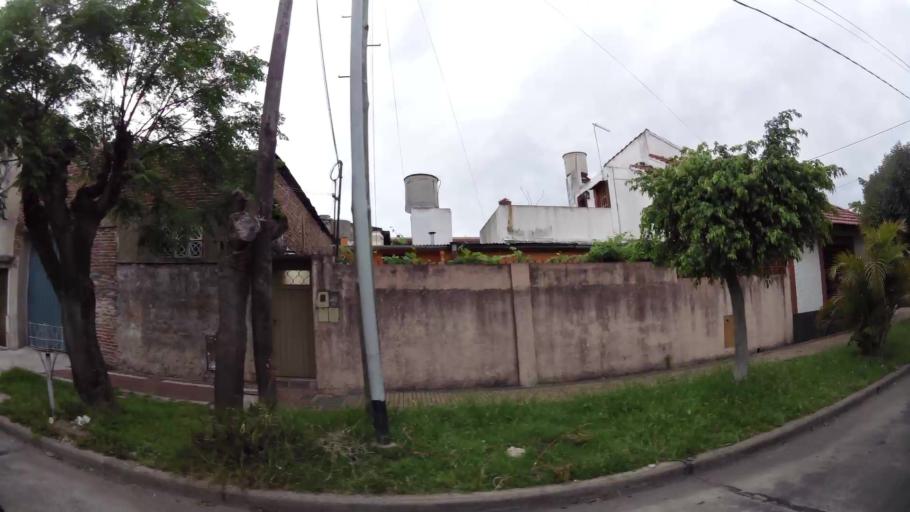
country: AR
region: Buenos Aires
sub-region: Partido de Lanus
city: Lanus
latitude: -34.6900
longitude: -58.3730
